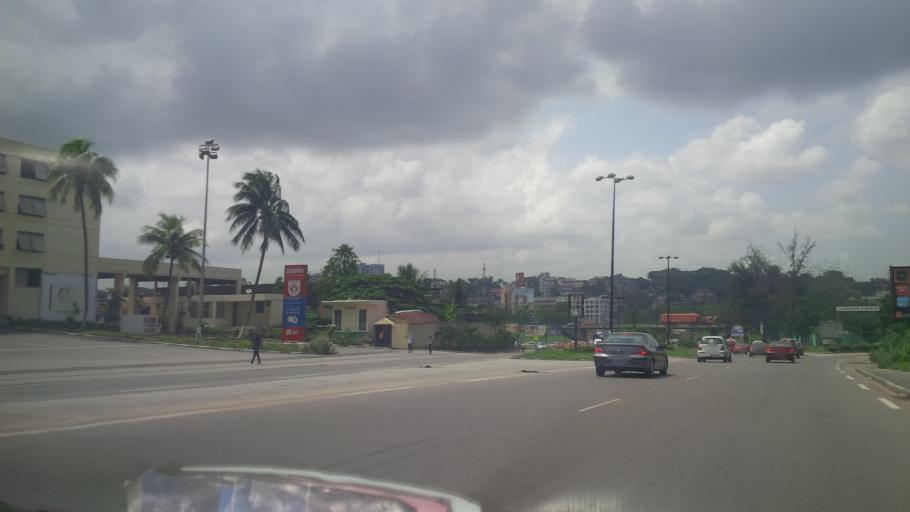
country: CI
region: Lagunes
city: Abidjan
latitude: 5.3412
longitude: -4.0203
